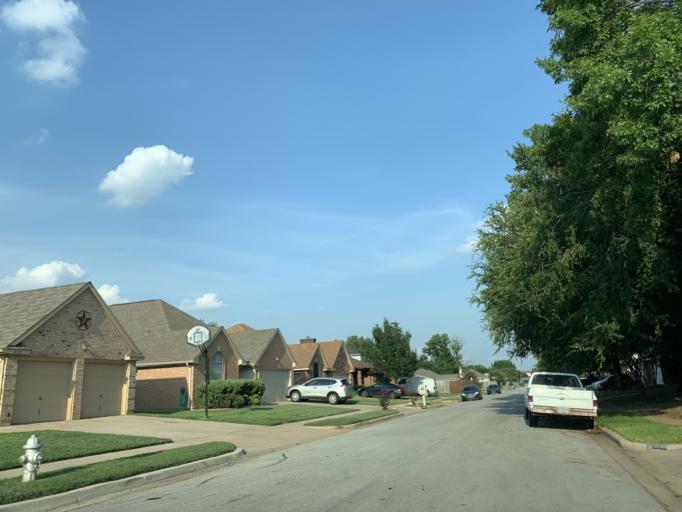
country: US
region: Texas
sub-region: Tarrant County
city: Hurst
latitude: 32.8019
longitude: -97.1903
